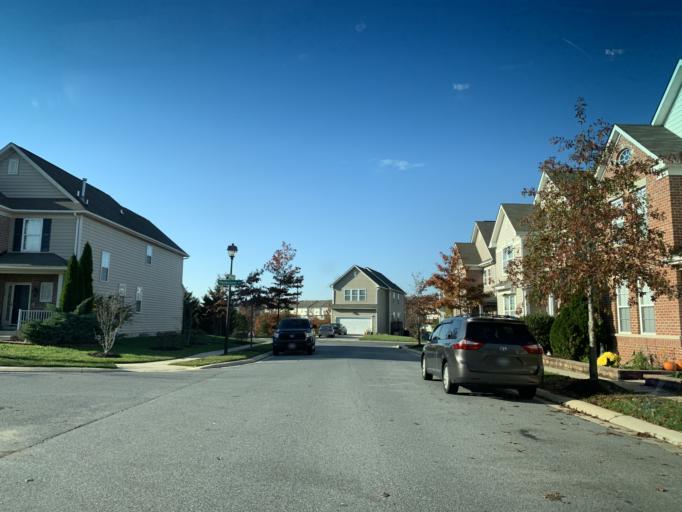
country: US
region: Maryland
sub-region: Baltimore County
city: Middle River
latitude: 39.3432
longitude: -76.4466
